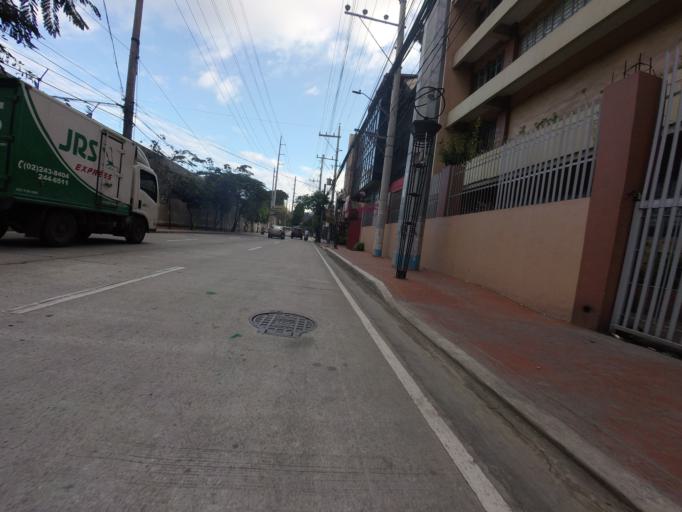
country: PH
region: Metro Manila
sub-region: City of Manila
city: Quiapo
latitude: 14.5824
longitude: 120.9874
